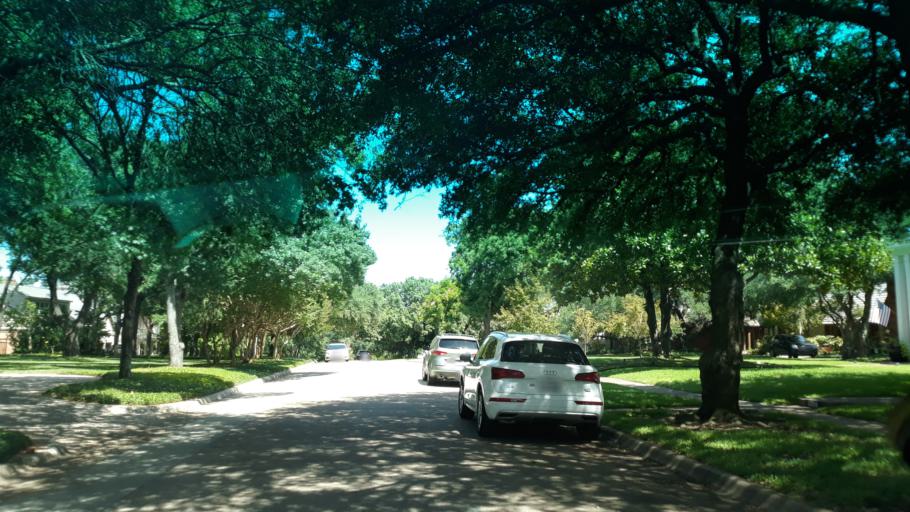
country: US
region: Texas
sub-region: Dallas County
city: Highland Park
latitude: 32.8180
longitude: -96.7435
